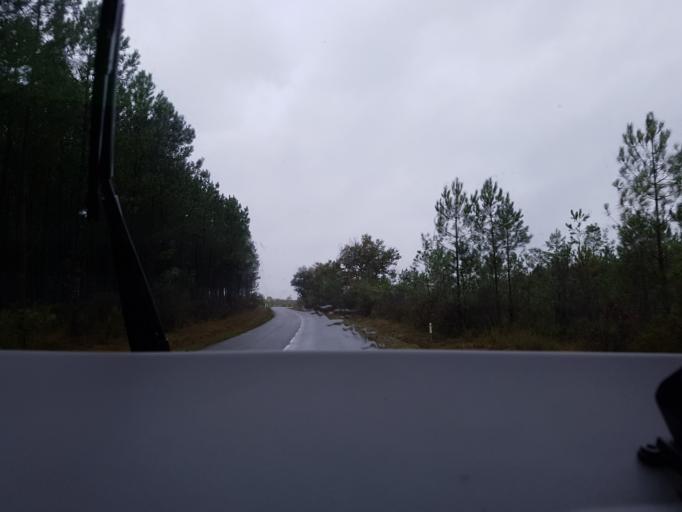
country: FR
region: Aquitaine
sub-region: Departement de la Gironde
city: Belin-Beliet
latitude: 44.4947
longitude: -0.6786
